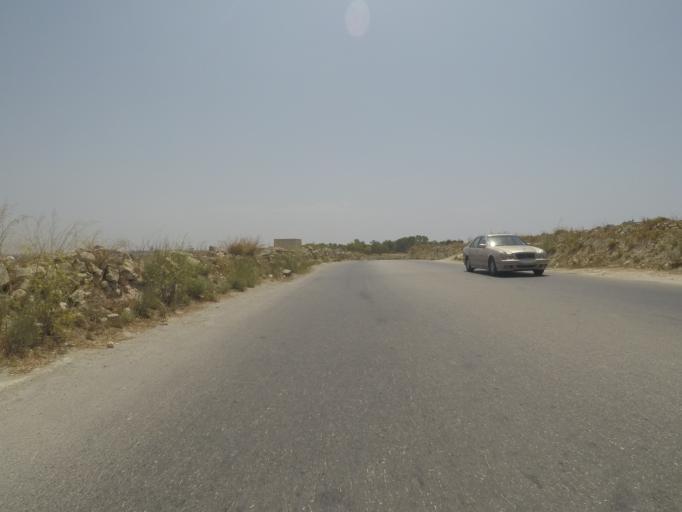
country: MT
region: Is-Siggiewi
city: Siggiewi
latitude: 35.8635
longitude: 14.4183
